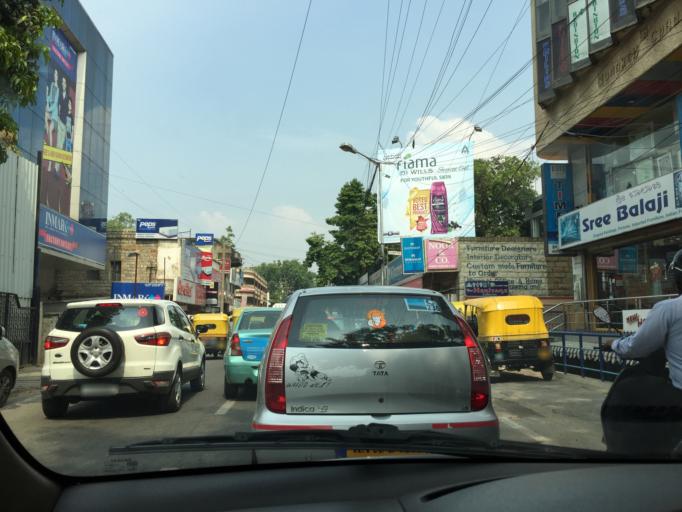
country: IN
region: Karnataka
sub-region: Bangalore Urban
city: Bangalore
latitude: 12.9810
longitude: 77.6021
